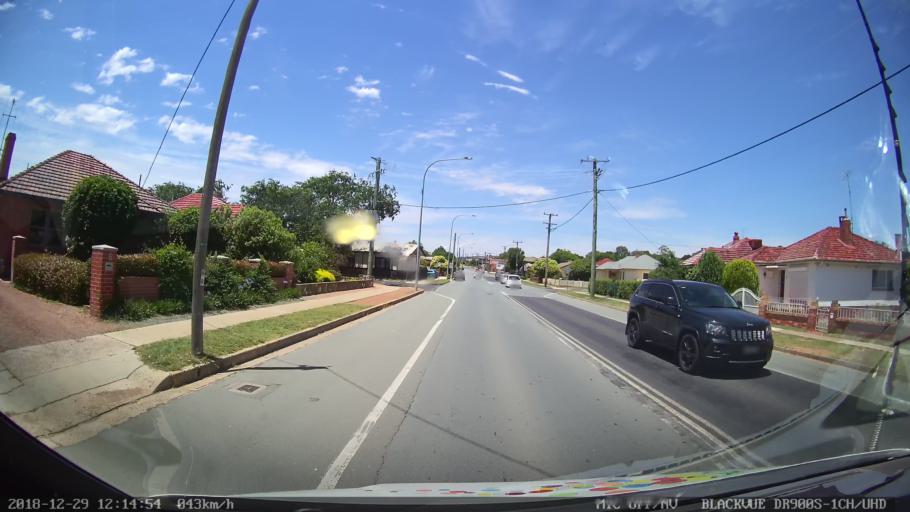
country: AU
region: New South Wales
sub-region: Queanbeyan
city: Queanbeyan
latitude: -35.3581
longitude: 149.2331
